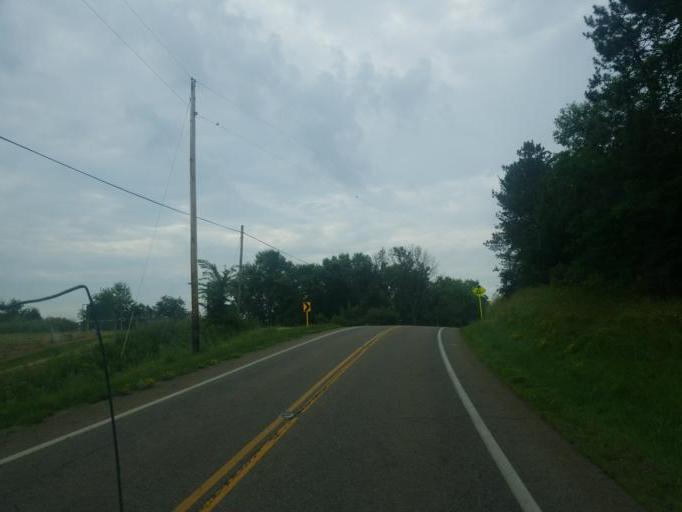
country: US
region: Ohio
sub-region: Carroll County
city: Lake Mohawk
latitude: 40.6458
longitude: -81.2301
